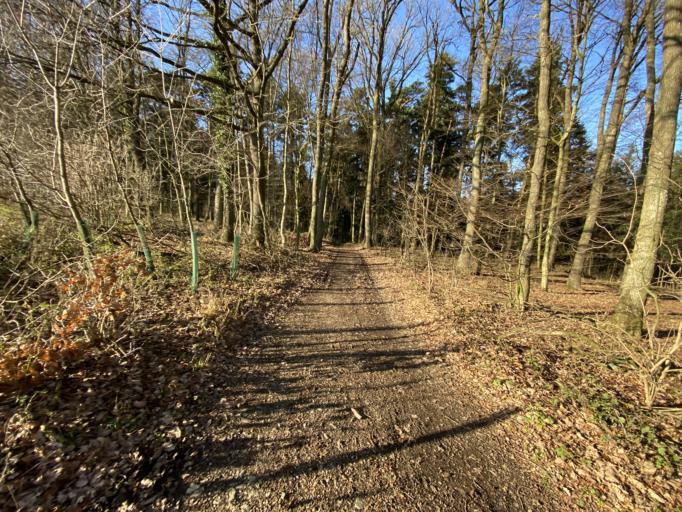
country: AT
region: Lower Austria
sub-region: Politischer Bezirk Sankt Polten
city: Boheimkirchen
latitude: 48.2033
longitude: 15.7455
